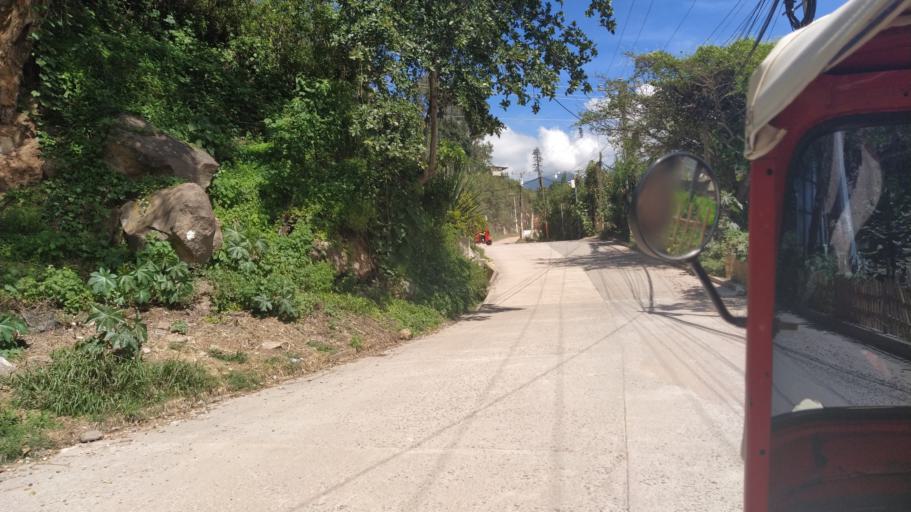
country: GT
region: Solola
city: San Pedro La Laguna
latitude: 14.6929
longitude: -91.2775
